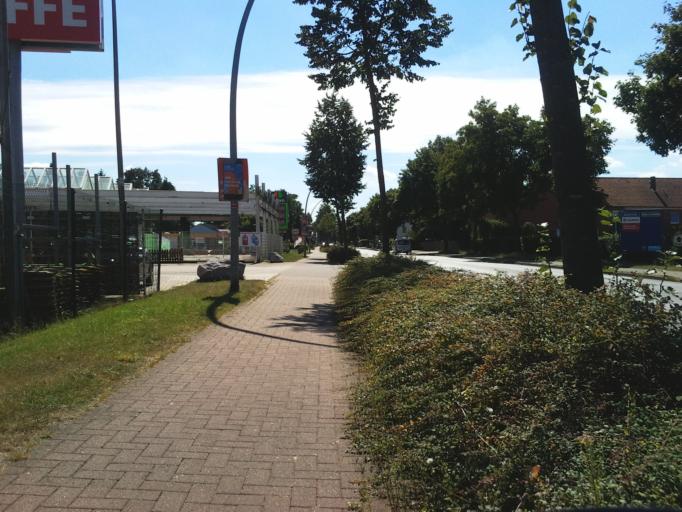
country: DE
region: Lower Saxony
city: Drakenburg
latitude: 52.6687
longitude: 9.2243
